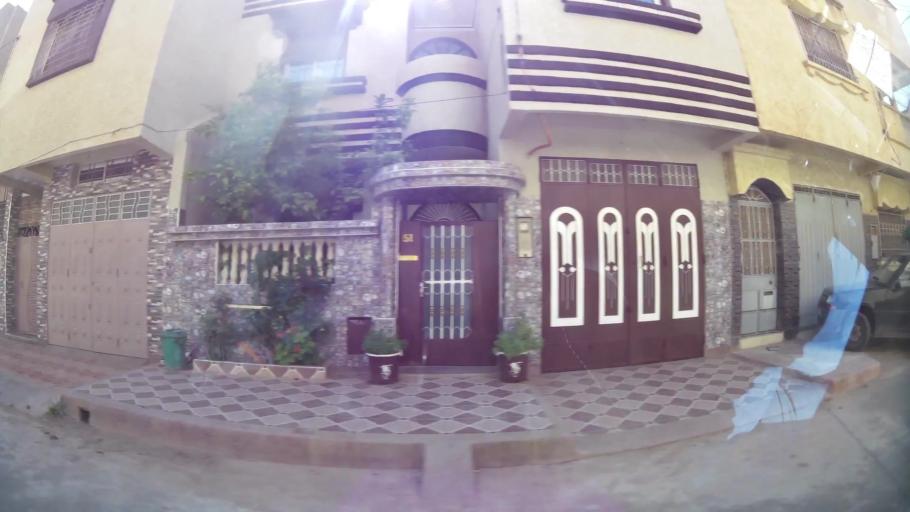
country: MA
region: Oriental
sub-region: Oujda-Angad
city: Oujda
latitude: 34.6887
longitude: -1.8710
